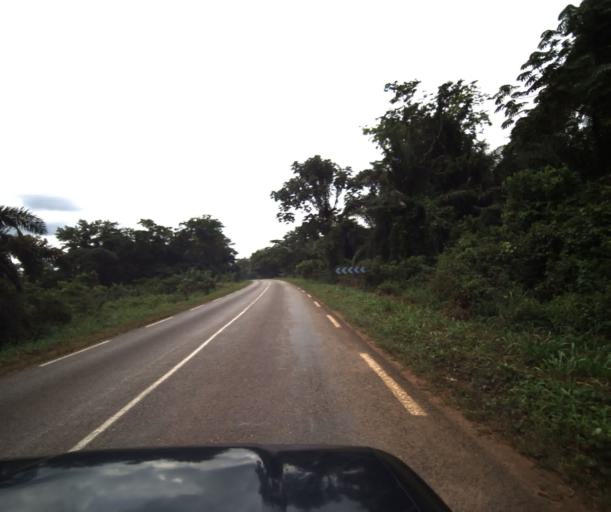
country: CM
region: Centre
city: Eseka
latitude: 3.8501
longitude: 10.4914
